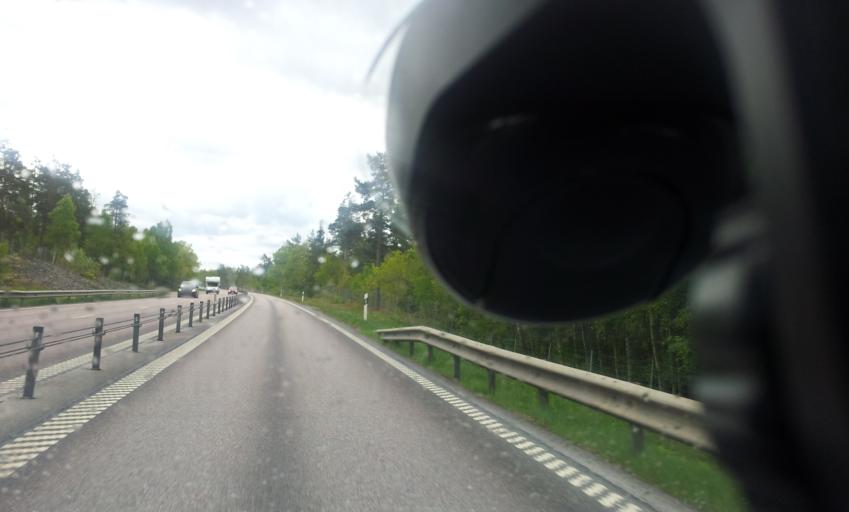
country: SE
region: Kalmar
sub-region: Oskarshamns Kommun
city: Paskallavik
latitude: 57.2142
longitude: 16.4346
